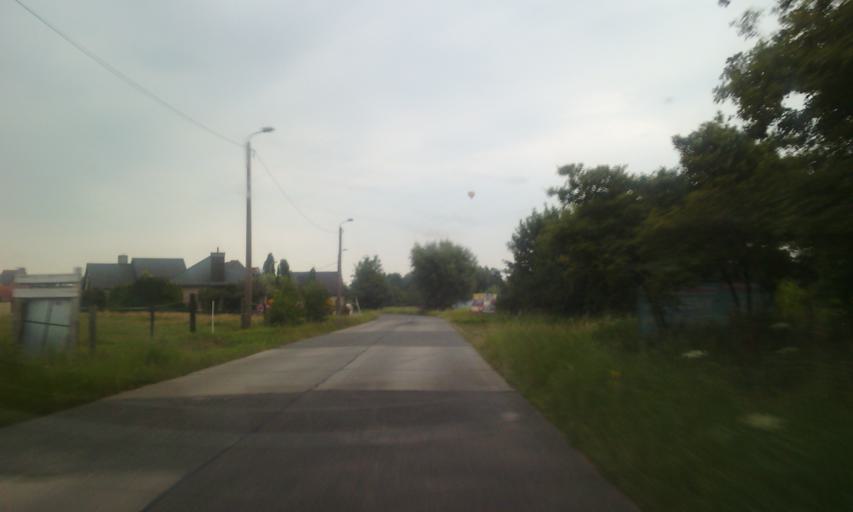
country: BE
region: Flanders
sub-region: Provincie Oost-Vlaanderen
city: Waasmunster
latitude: 51.0713
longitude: 4.0884
